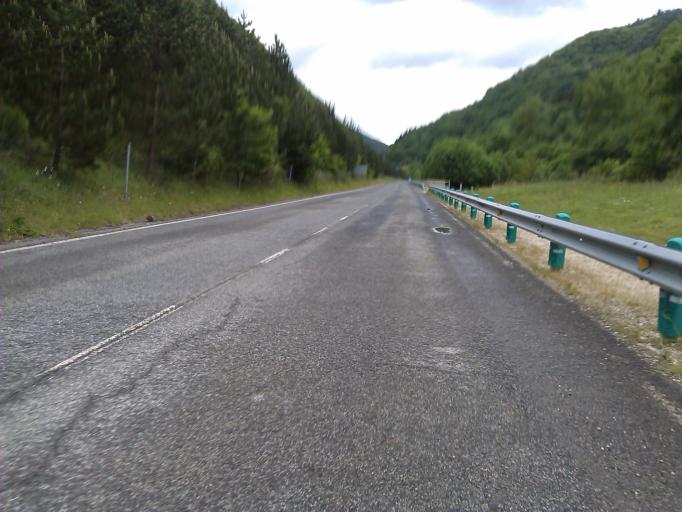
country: ES
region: Navarre
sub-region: Provincia de Navarra
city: Irurtzun
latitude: 42.9698
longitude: -1.8429
